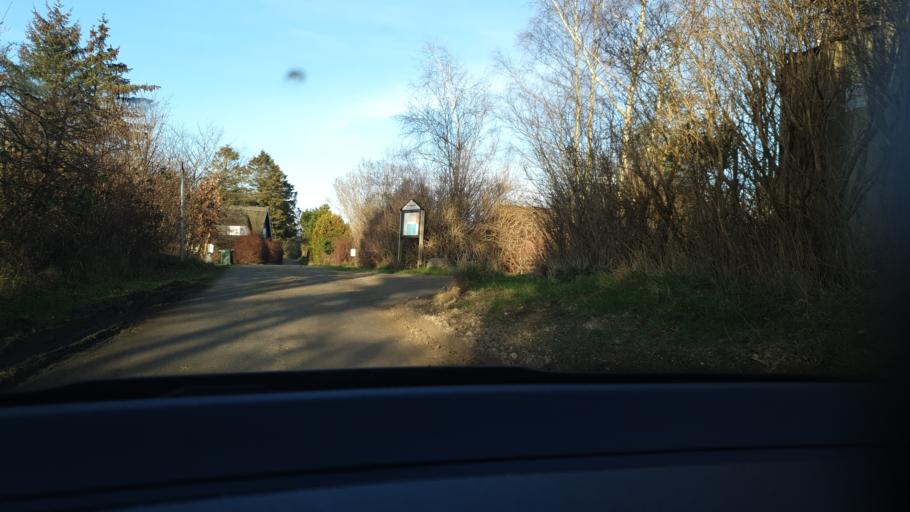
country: DK
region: Zealand
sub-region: Odsherred Kommune
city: Hojby
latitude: 55.9340
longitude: 11.6229
